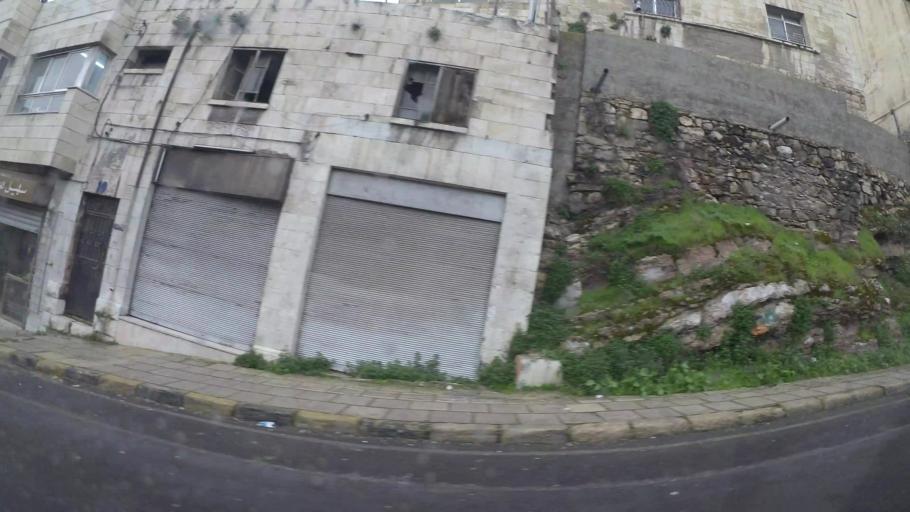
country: JO
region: Amman
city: Amman
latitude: 31.9515
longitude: 35.9265
